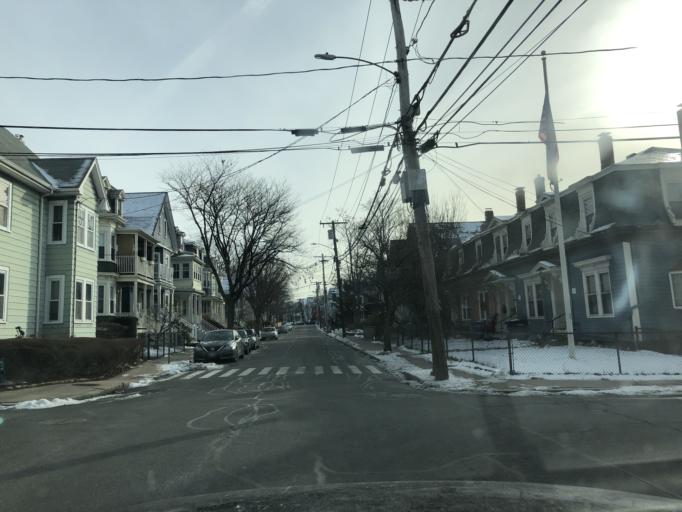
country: US
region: Massachusetts
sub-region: Middlesex County
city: Somerville
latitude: 42.3965
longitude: -71.1177
